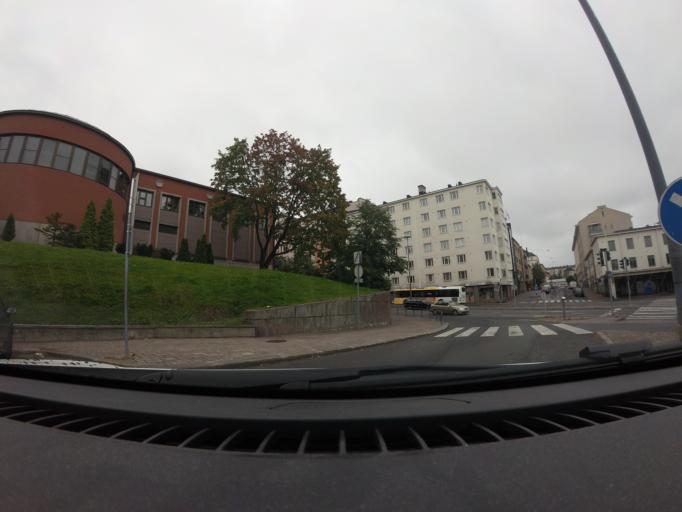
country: FI
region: Varsinais-Suomi
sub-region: Turku
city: Turku
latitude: 60.4564
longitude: 22.2694
